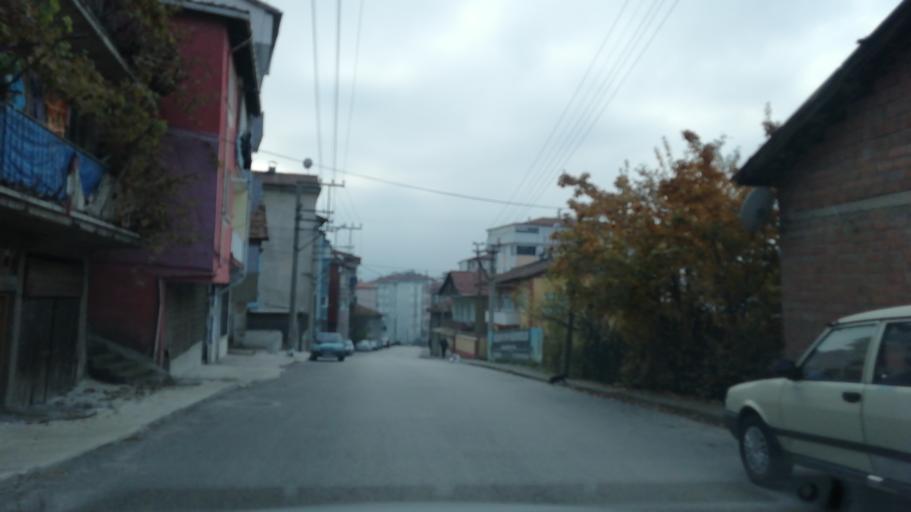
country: TR
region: Karabuk
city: Karabuk
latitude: 41.2093
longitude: 32.6273
